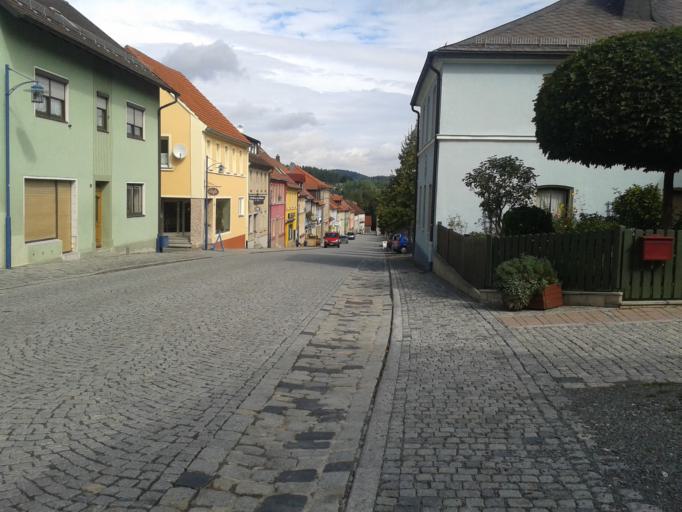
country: DE
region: Bavaria
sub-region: Upper Franconia
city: Marktschorgast
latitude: 50.0941
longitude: 11.6547
